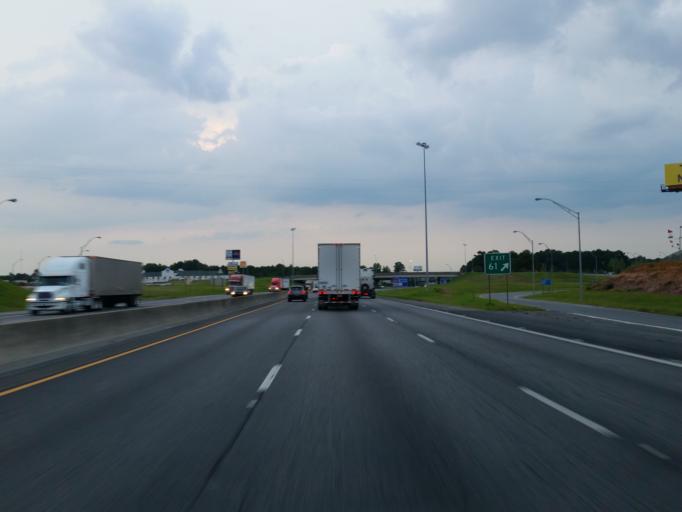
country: US
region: Georgia
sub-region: Tift County
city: Unionville
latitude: 31.4387
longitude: -83.5247
